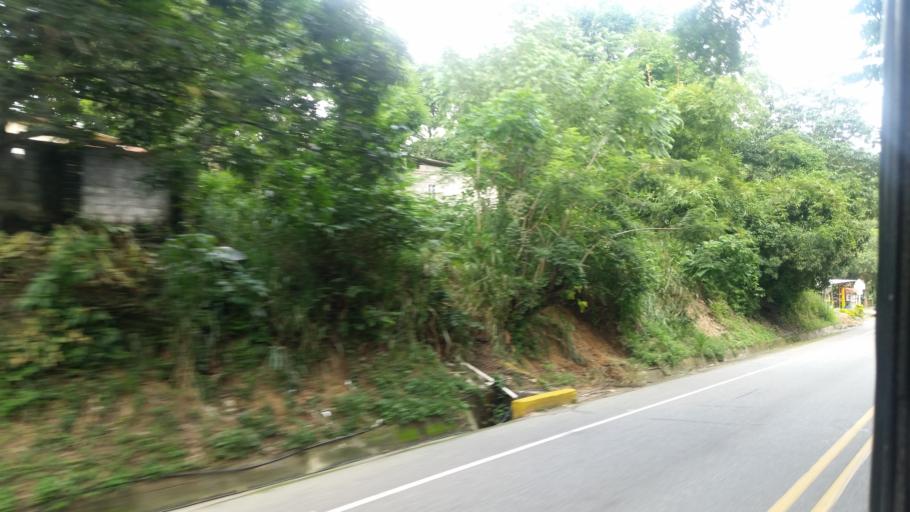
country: CO
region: Magdalena
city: Santa Marta
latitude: 11.2784
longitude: -74.0305
